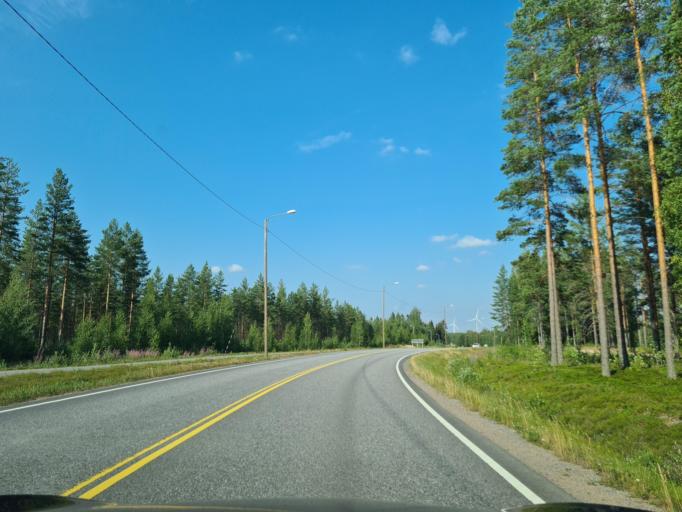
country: FI
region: Satakunta
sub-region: Pohjois-Satakunta
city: Karvia
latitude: 62.0745
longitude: 22.5072
